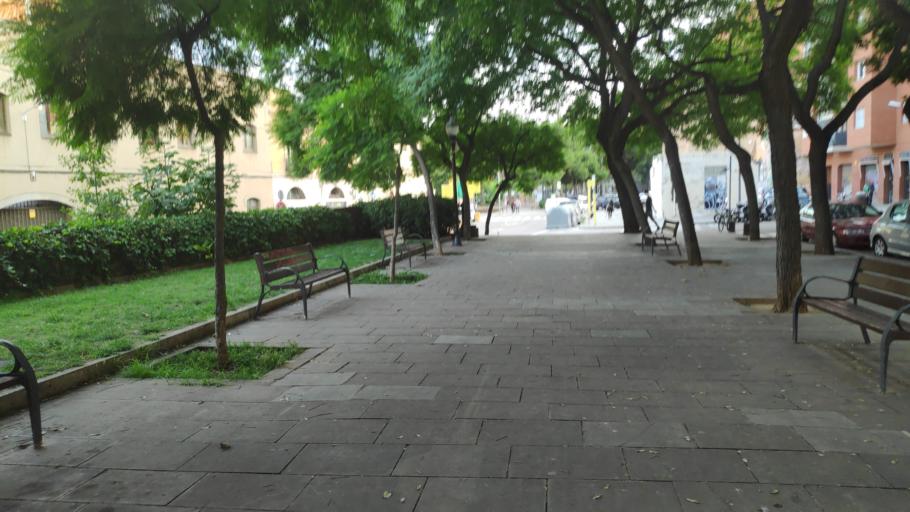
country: ES
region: Catalonia
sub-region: Provincia de Barcelona
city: Sant Marti
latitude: 41.4100
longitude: 2.1904
